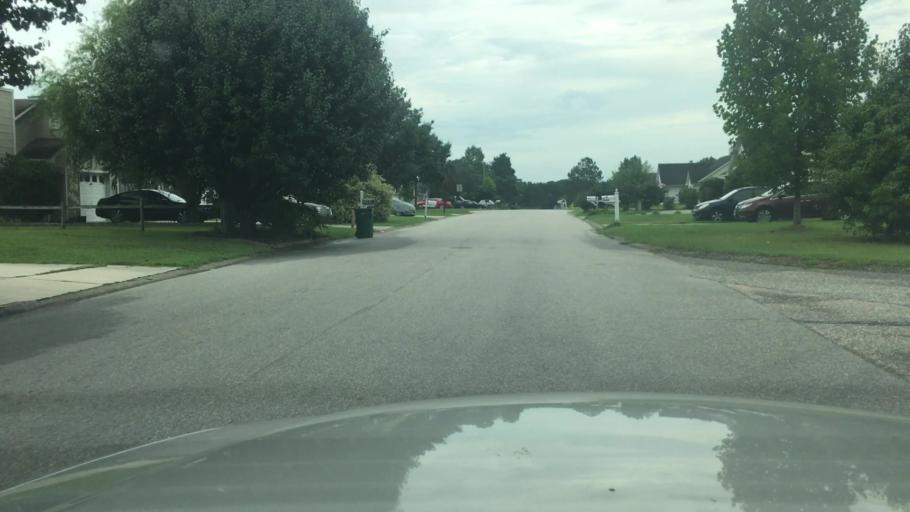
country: US
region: North Carolina
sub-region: Cumberland County
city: Hope Mills
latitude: 34.9956
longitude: -78.9748
